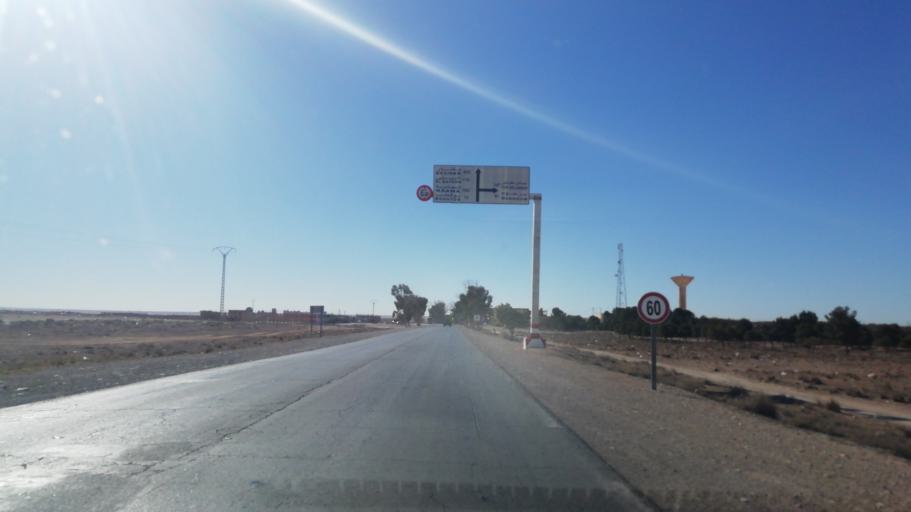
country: DZ
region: Saida
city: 'Ain el Hadjar
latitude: 34.1598
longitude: 0.0713
